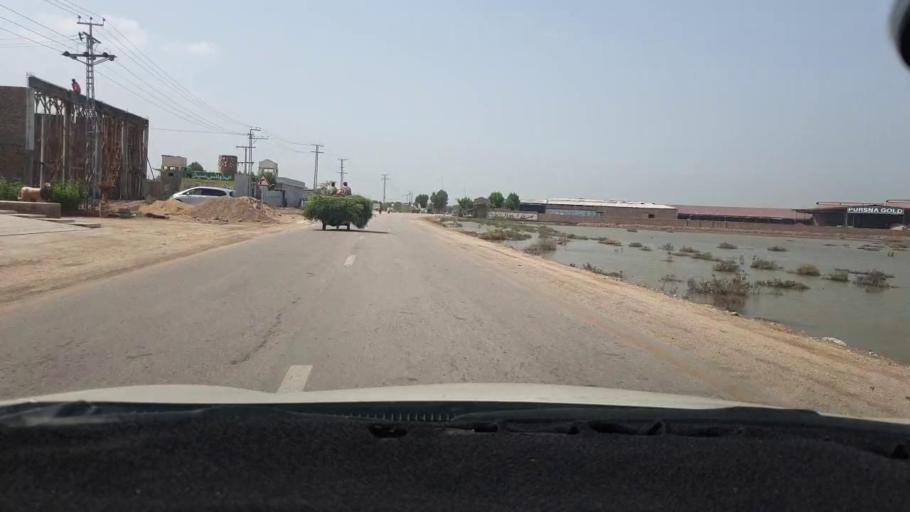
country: PK
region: Sindh
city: Mirpur Khas
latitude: 25.5504
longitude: 69.0478
